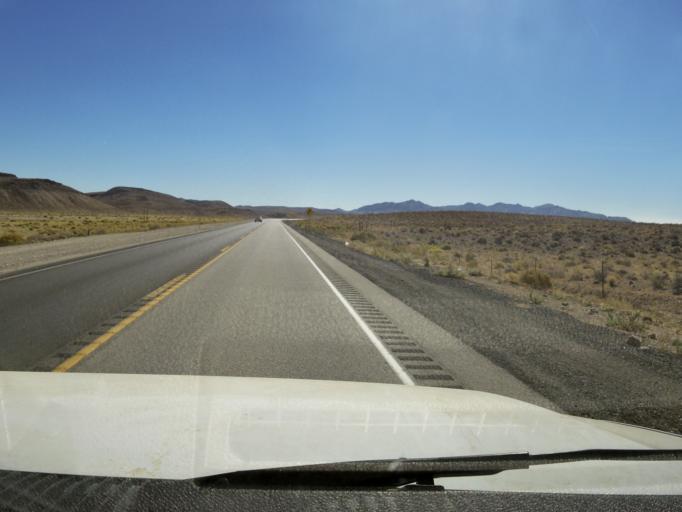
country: US
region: Nevada
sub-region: Nye County
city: Beatty
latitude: 37.0151
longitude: -116.7311
